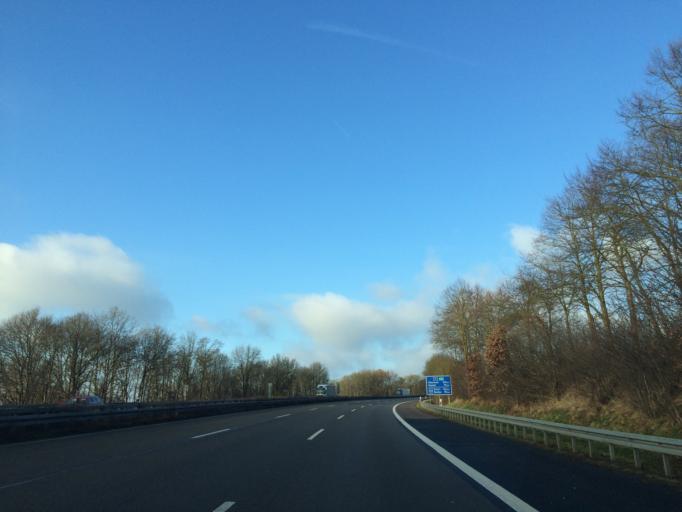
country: DE
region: Hesse
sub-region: Regierungsbezirk Kassel
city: Niederaula
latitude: 50.7784
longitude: 9.5771
